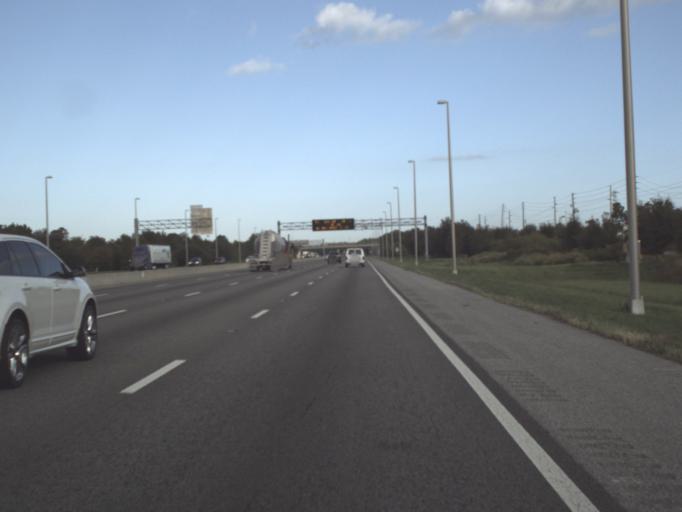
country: US
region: Florida
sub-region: Orange County
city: Oak Ridge
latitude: 28.4446
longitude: -81.4168
